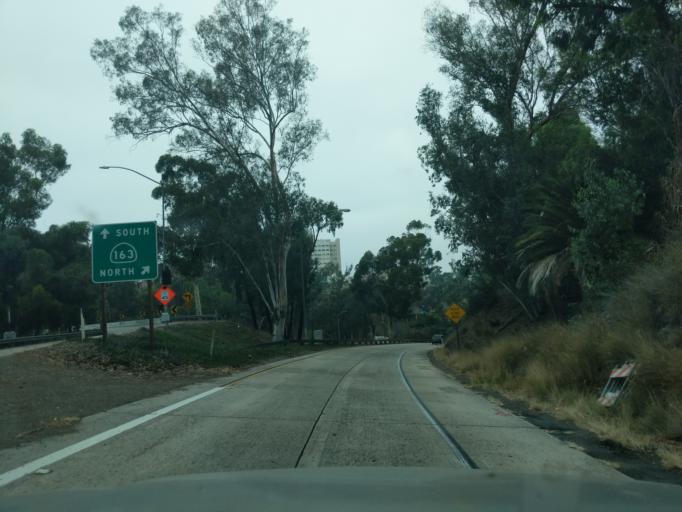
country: US
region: California
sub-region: San Diego County
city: San Diego
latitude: 32.7514
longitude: -117.1543
